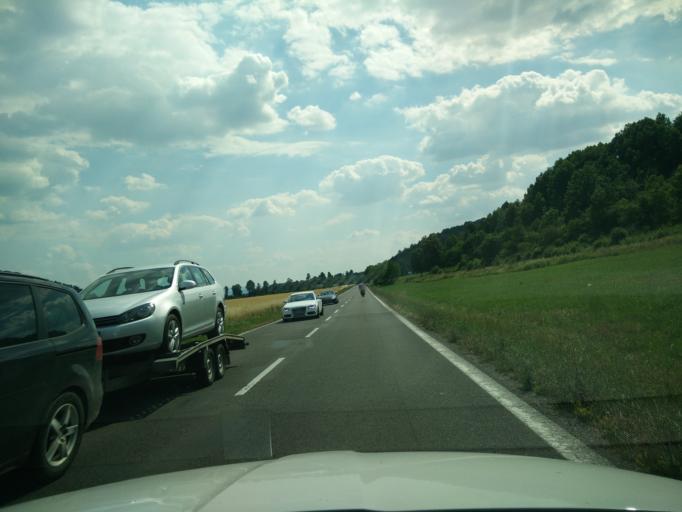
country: SK
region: Nitriansky
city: Partizanske
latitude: 48.6993
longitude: 18.3882
